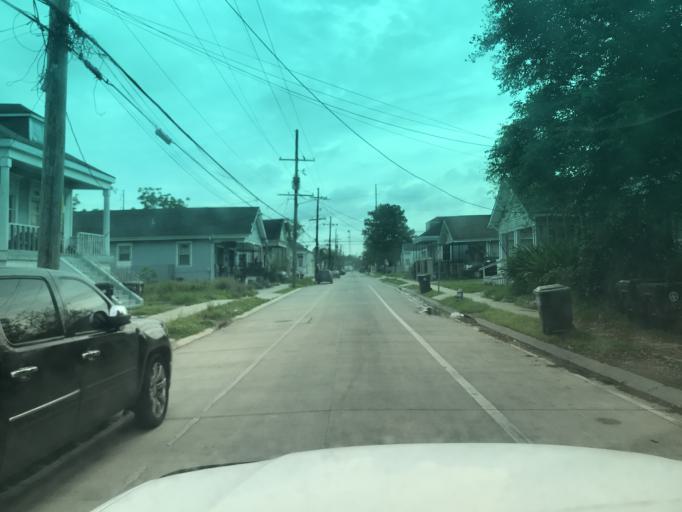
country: US
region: Louisiana
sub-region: Orleans Parish
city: New Orleans
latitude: 29.9790
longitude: -90.0516
